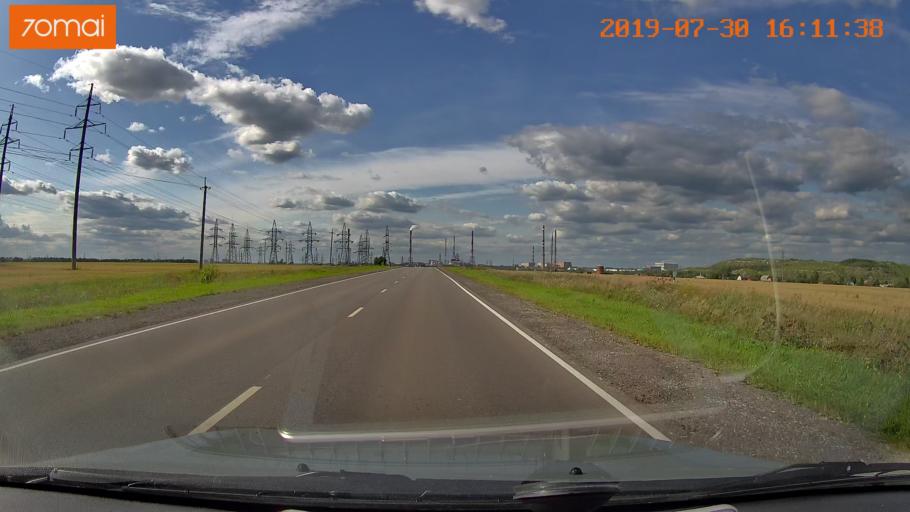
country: RU
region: Moskovskaya
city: Lopatinskiy
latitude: 55.2793
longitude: 38.7084
